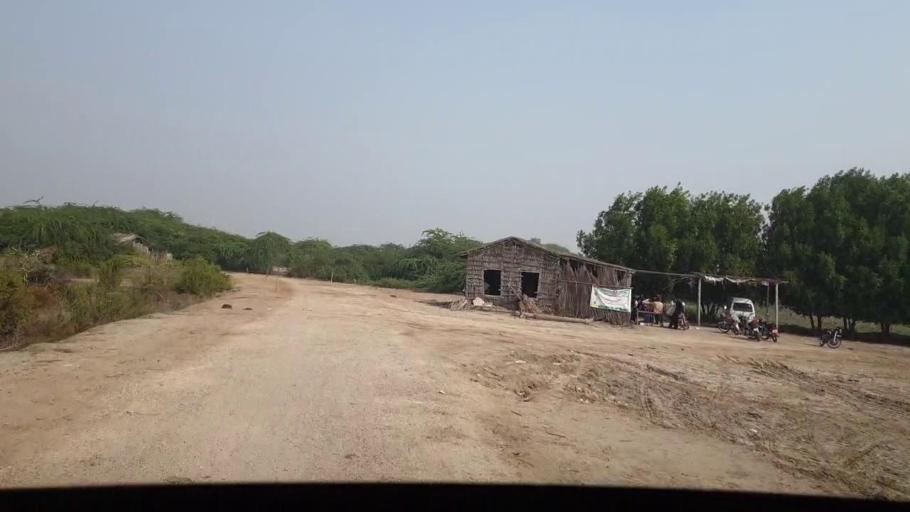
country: PK
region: Sindh
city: Jati
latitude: 24.4360
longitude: 68.4388
